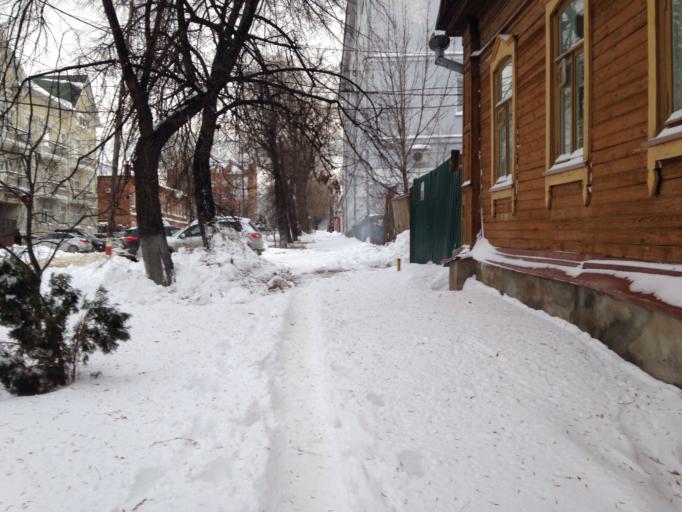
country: RU
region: Ulyanovsk
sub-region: Ulyanovskiy Rayon
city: Ulyanovsk
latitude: 54.3160
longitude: 48.3967
